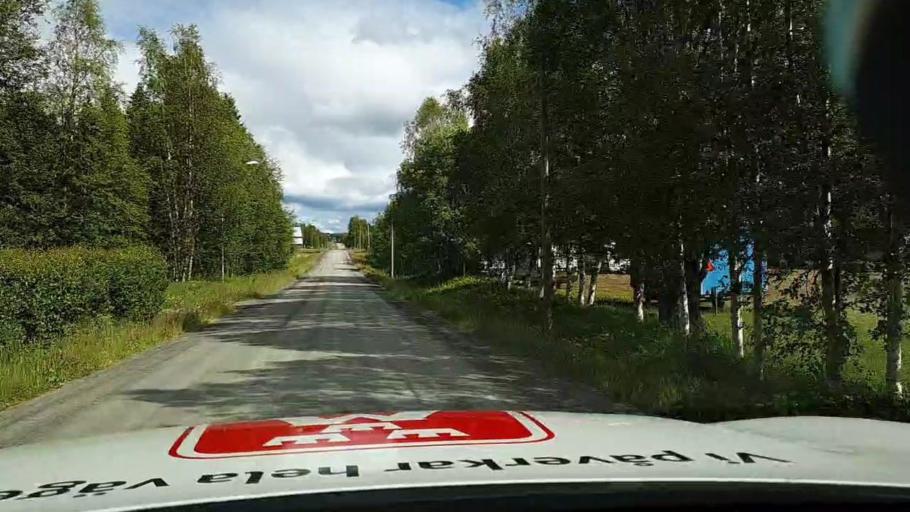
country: SE
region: Jaemtland
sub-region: Krokoms Kommun
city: Valla
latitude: 63.6969
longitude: 13.6256
